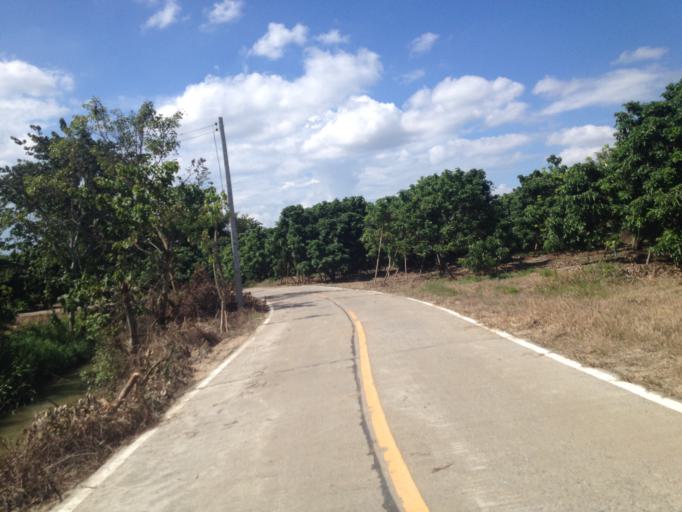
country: TH
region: Chiang Mai
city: Saraphi
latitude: 18.6981
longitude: 98.9806
